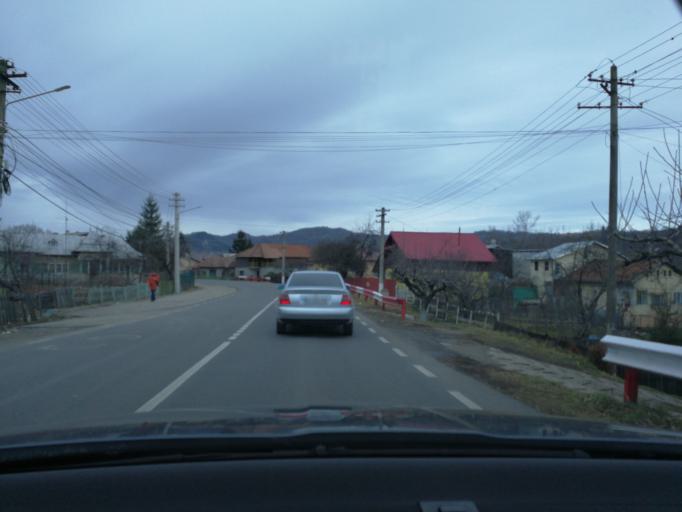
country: RO
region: Prahova
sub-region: Comuna Cornu
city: Cornu de Jos
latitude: 45.1474
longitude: 25.6918
